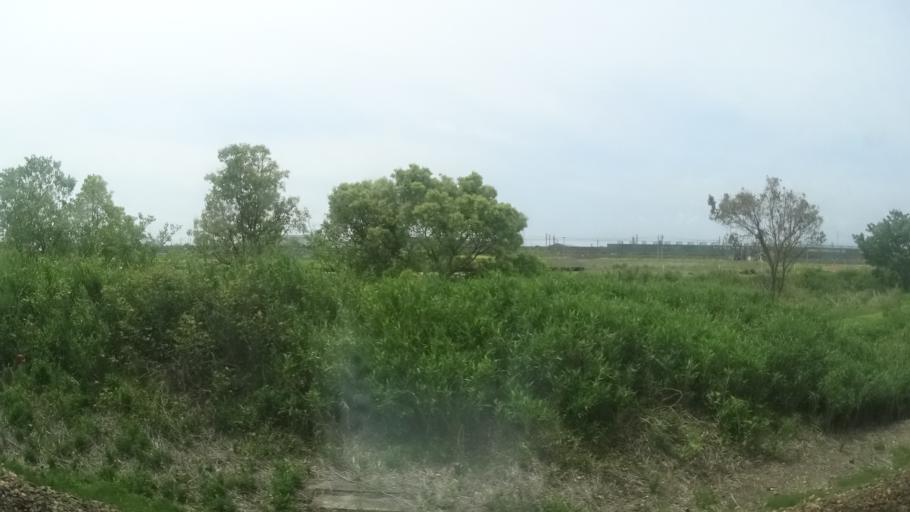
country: JP
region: Shizuoka
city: Kosai-shi
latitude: 34.7226
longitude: 137.4627
